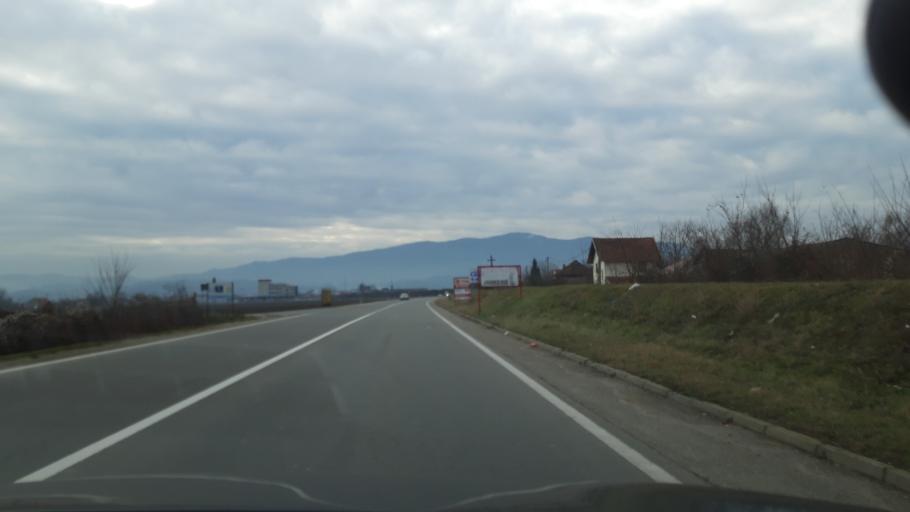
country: RS
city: Lipnicki Sor
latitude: 44.5562
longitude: 19.1991
